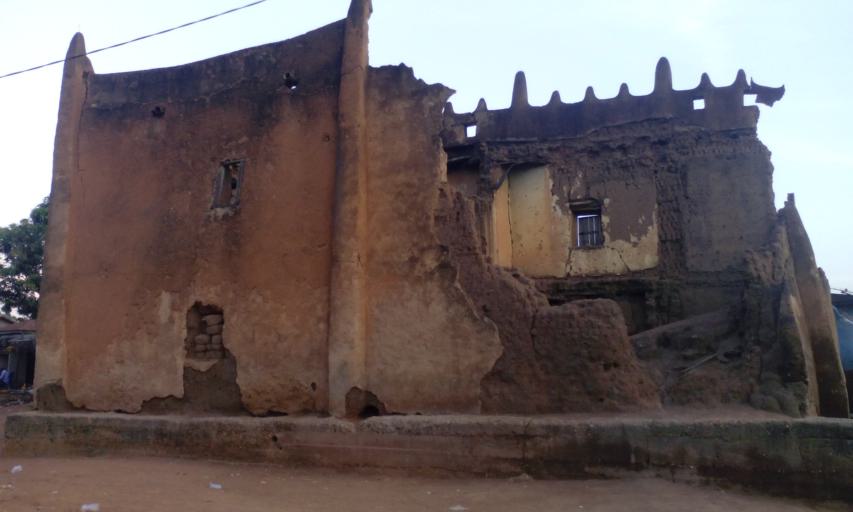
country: CI
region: Zanzan
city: Bondoukou
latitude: 8.0387
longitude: -2.7964
